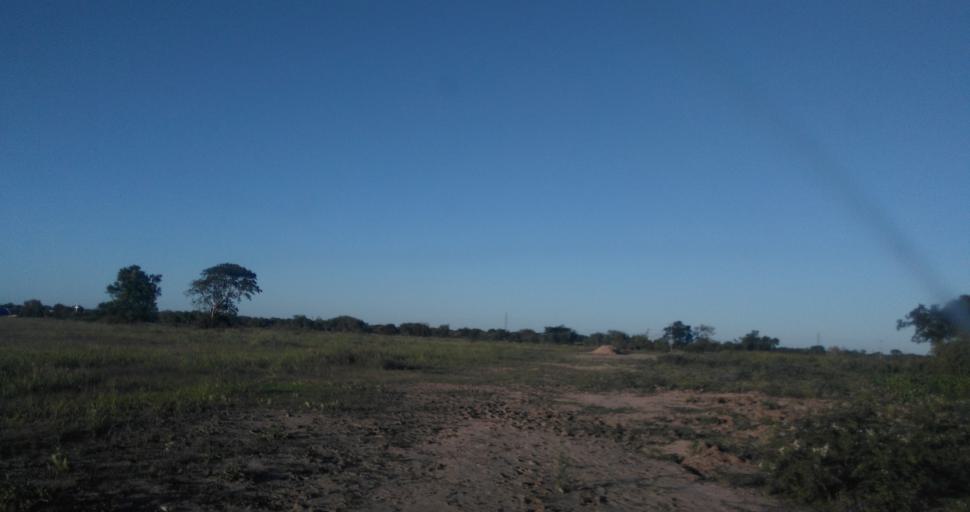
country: AR
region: Chaco
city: Fontana
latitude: -27.3943
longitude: -58.9826
